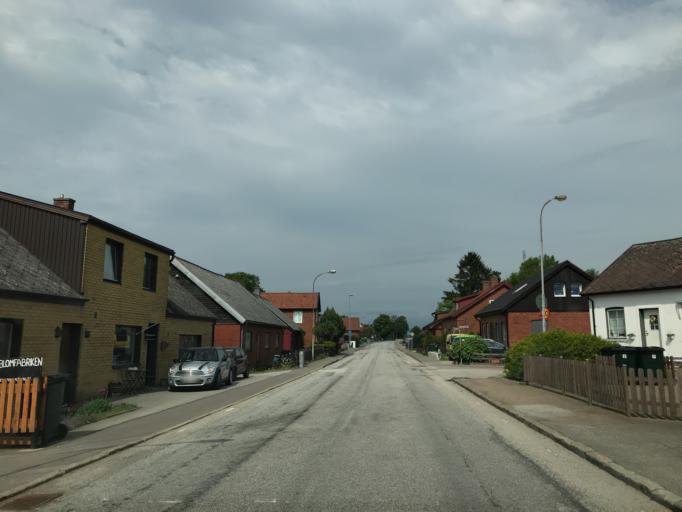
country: SE
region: Skane
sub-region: Svalovs Kommun
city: Svaloev
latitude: 55.8662
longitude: 13.1526
